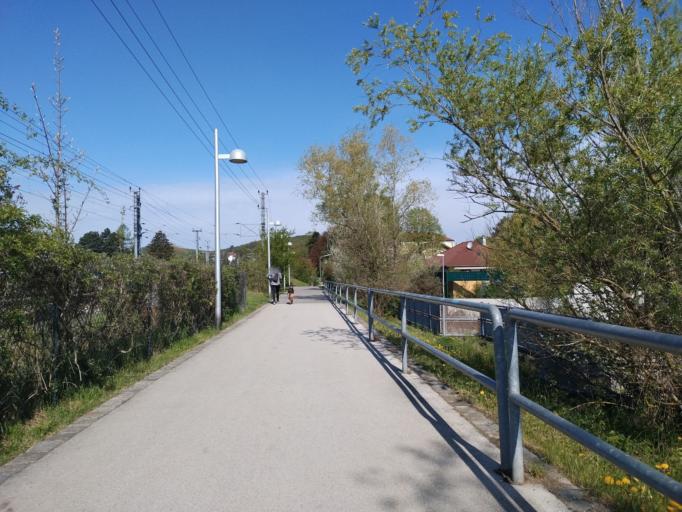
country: AT
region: Lower Austria
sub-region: Politischer Bezirk Wien-Umgebung
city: Purkersdorf
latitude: 48.2096
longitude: 16.2290
